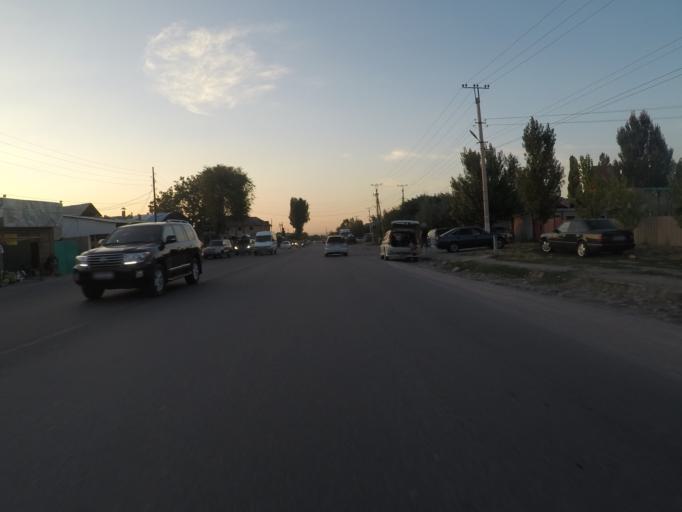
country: KG
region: Chuy
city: Lebedinovka
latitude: 42.8079
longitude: 74.6470
